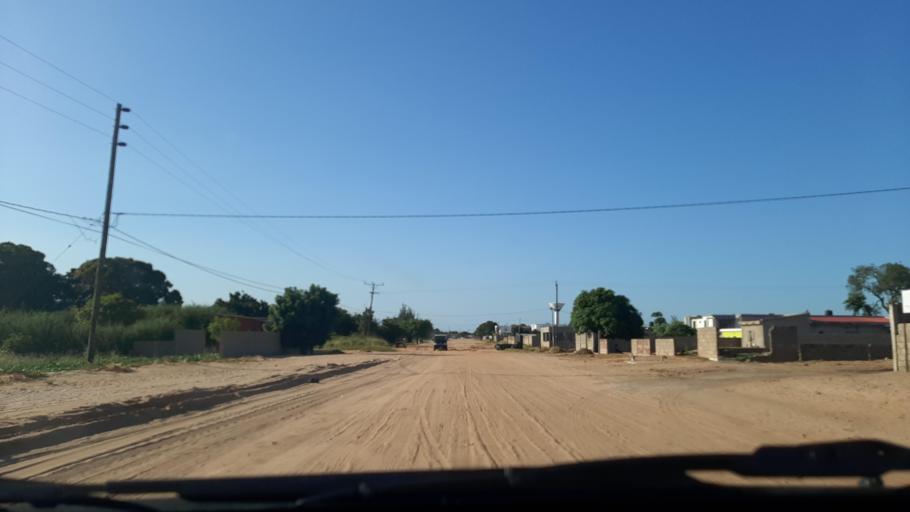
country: MZ
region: Maputo City
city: Maputo
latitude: -25.7939
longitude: 32.5522
